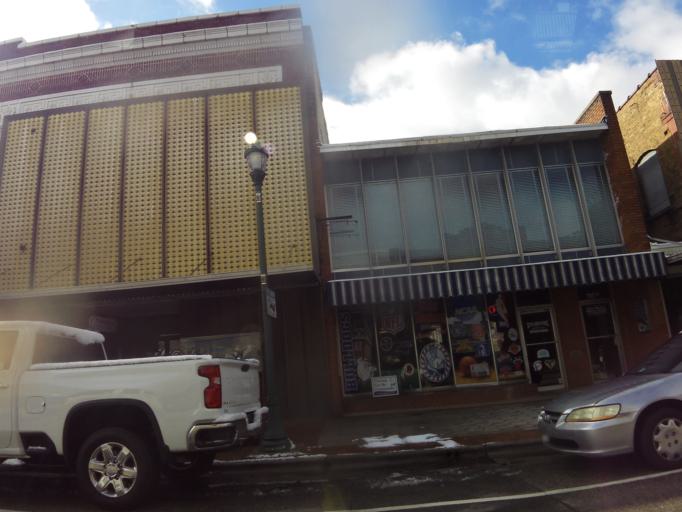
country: US
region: North Carolina
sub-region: Wilson County
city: Wilson
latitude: 35.7261
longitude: -77.9114
